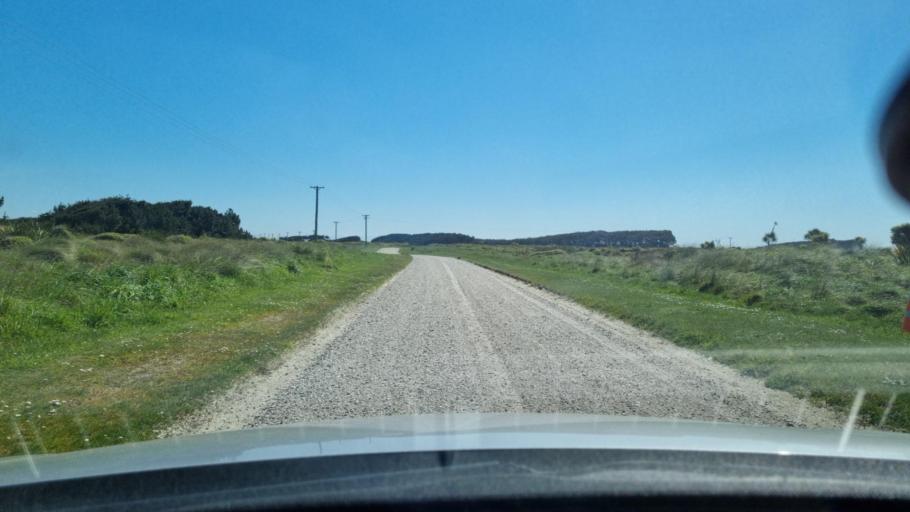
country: NZ
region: Southland
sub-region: Invercargill City
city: Invercargill
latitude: -46.4368
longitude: 168.2383
